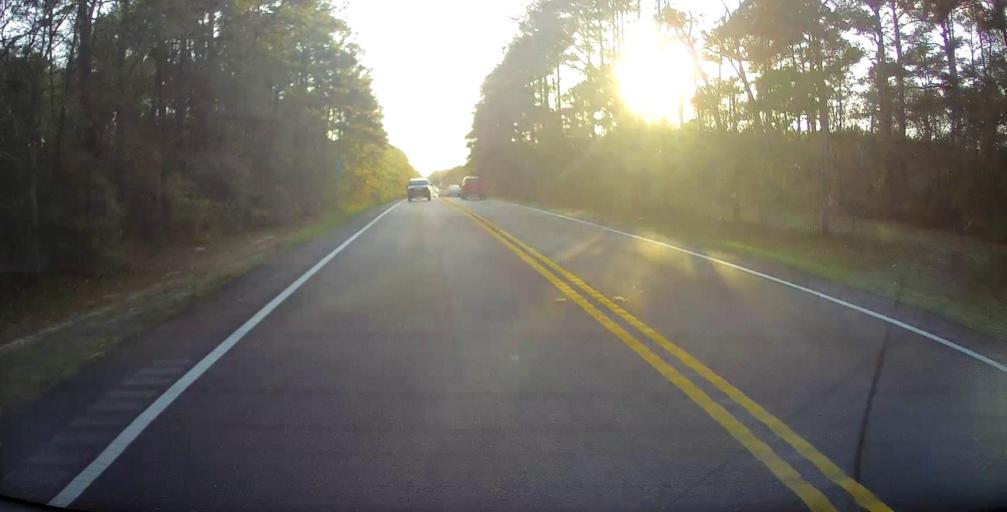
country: US
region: Georgia
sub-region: Bryan County
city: Pembroke
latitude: 32.1721
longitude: -81.4782
